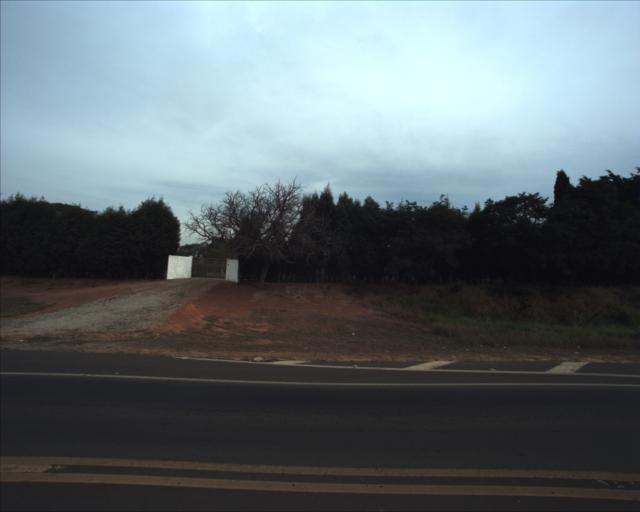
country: BR
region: Sao Paulo
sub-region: Sorocaba
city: Sorocaba
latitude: -23.4233
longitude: -47.5188
